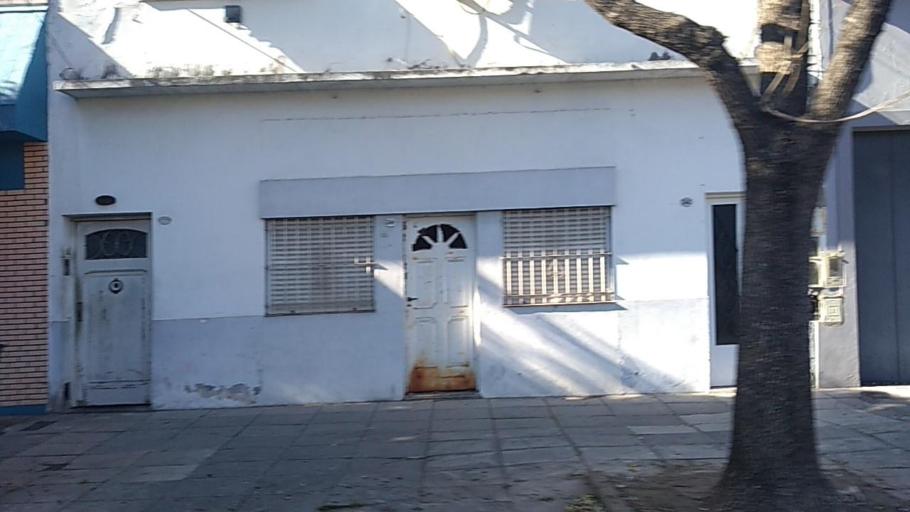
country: AR
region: Buenos Aires F.D.
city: Villa Santa Rita
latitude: -34.6187
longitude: -58.4929
